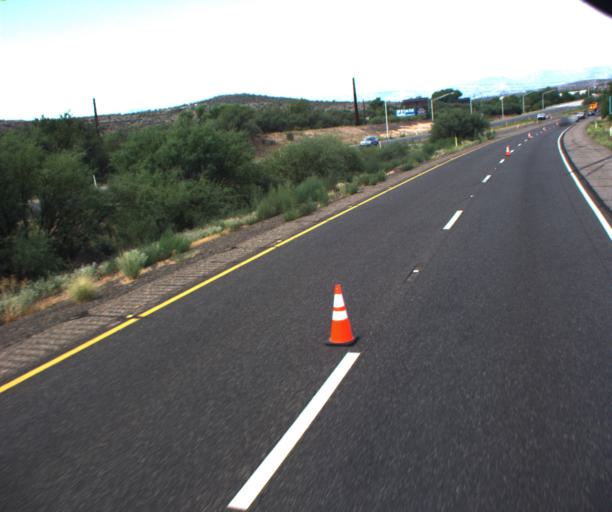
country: US
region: Arizona
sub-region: Yavapai County
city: Lake Montezuma
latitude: 34.6411
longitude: -111.8109
